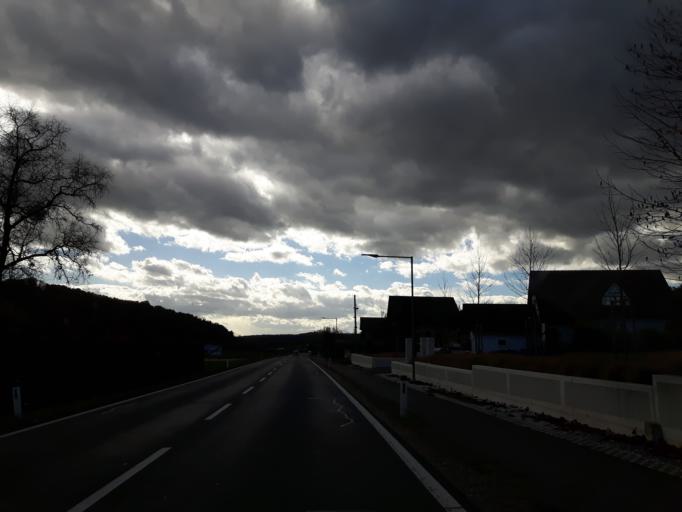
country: AT
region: Styria
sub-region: Politischer Bezirk Suedoststeiermark
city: Sankt Stefan im Rosental
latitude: 46.9245
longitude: 15.7169
